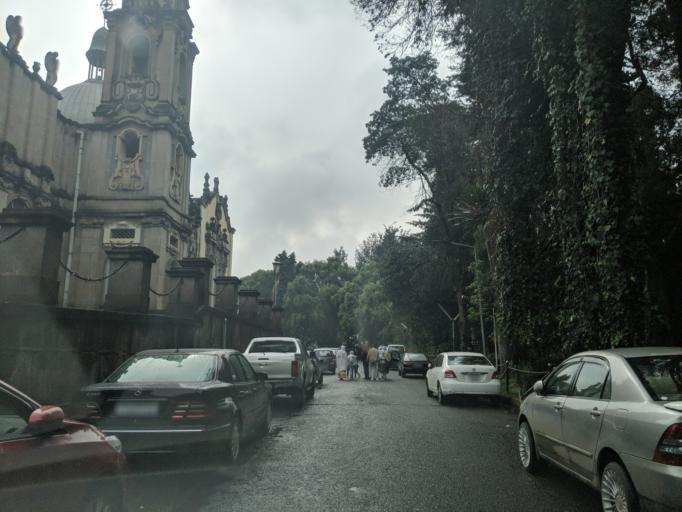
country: ET
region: Adis Abeba
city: Addis Ababa
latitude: 9.0306
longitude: 38.7662
